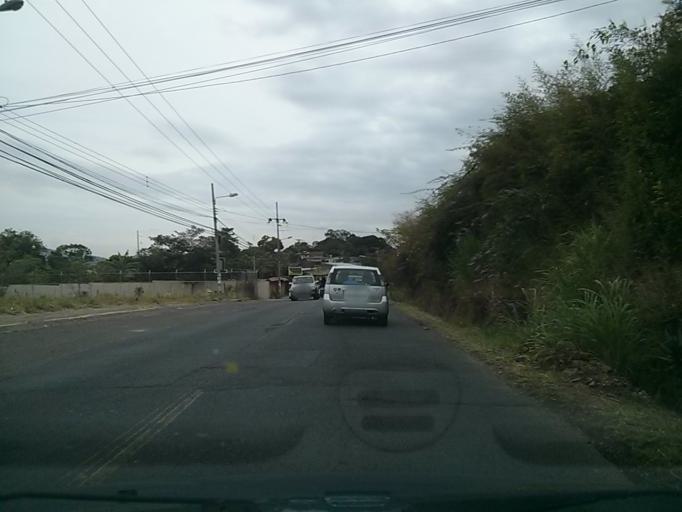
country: CR
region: San Jose
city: Patarra
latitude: 9.8917
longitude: -84.0416
